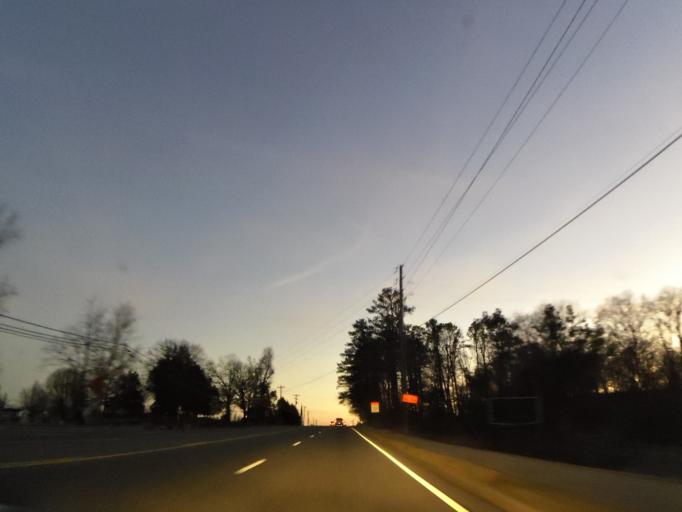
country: US
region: Georgia
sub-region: Whitfield County
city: Varnell
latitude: 34.8375
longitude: -84.9431
